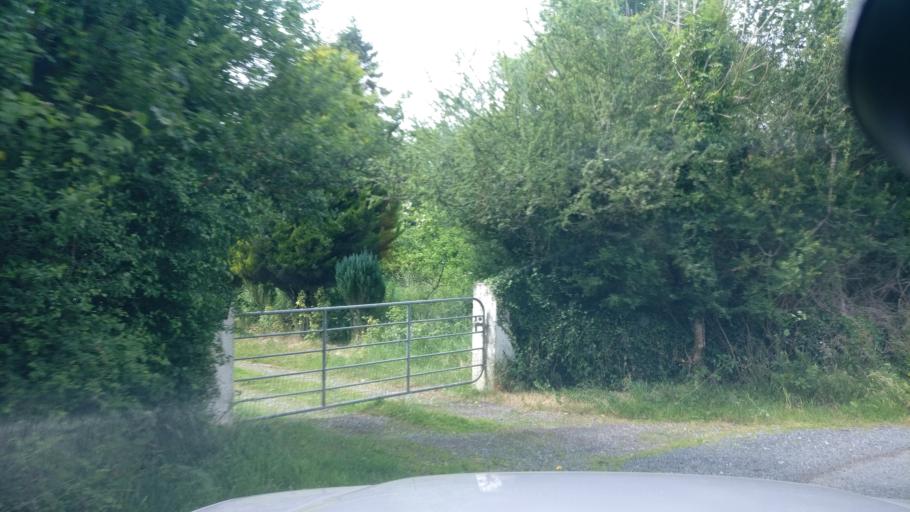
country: IE
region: Connaught
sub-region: County Galway
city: Ballinasloe
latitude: 53.2812
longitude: -8.3361
